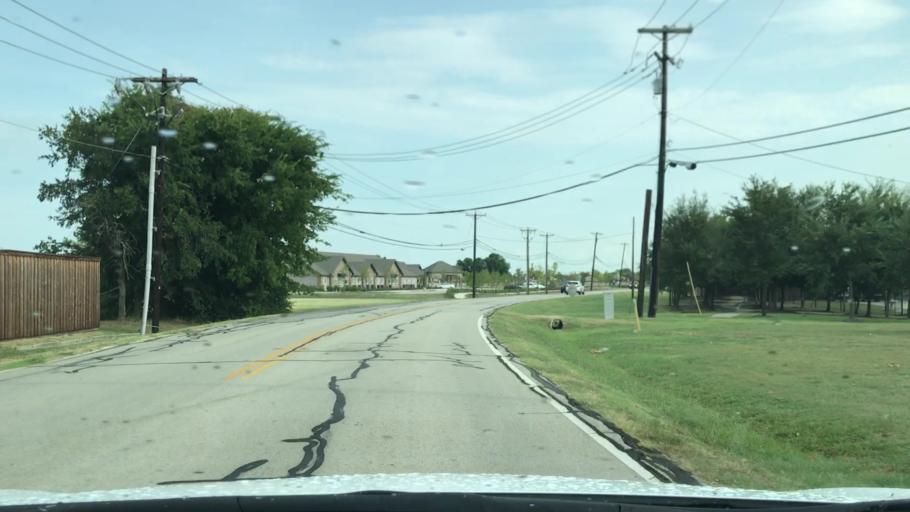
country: US
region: Texas
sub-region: Dallas County
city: Rowlett
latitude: 32.9319
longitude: -96.5365
